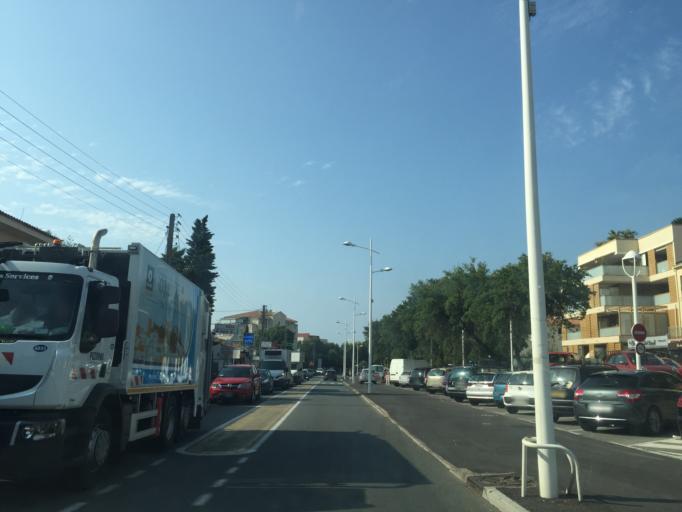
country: FR
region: Provence-Alpes-Cote d'Azur
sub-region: Departement du Var
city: Frejus
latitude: 43.3839
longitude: 6.7223
